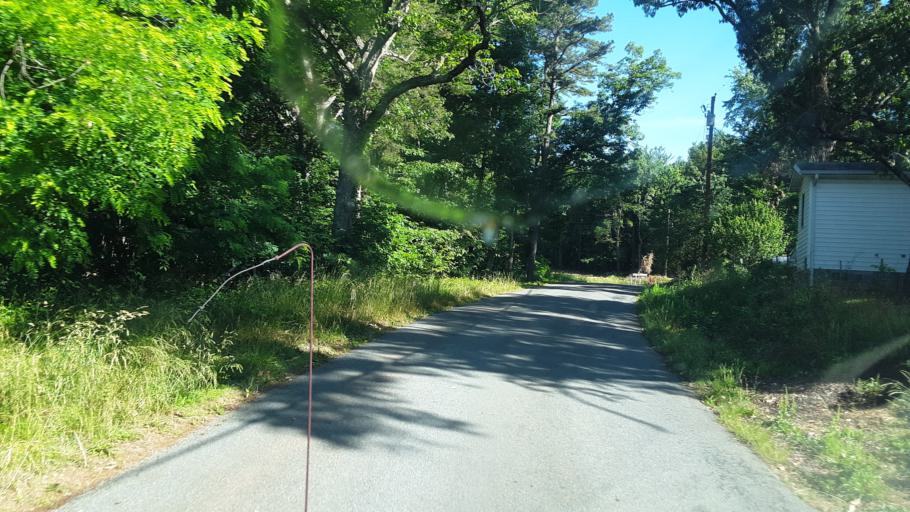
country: US
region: Virginia
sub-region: Pittsylvania County
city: Chatham
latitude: 36.8378
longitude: -79.3981
